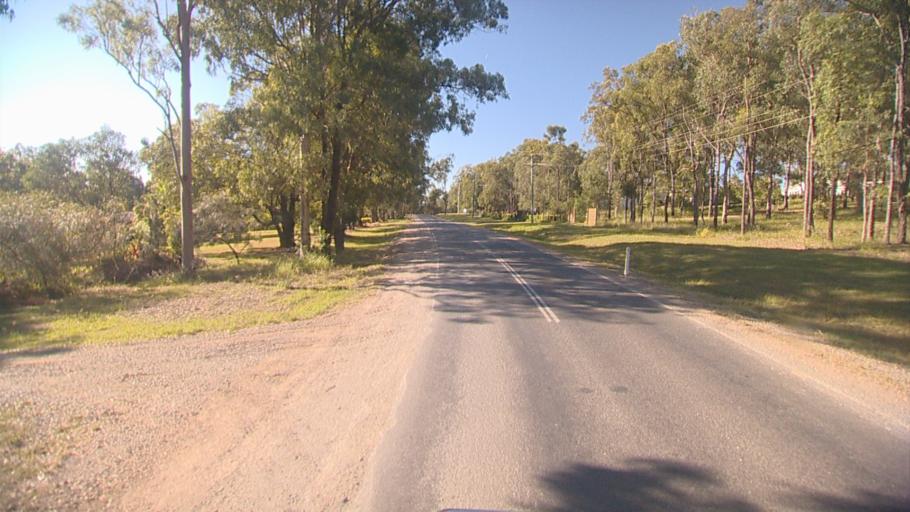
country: AU
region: Queensland
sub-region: Logan
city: Waterford West
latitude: -27.7444
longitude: 153.1423
